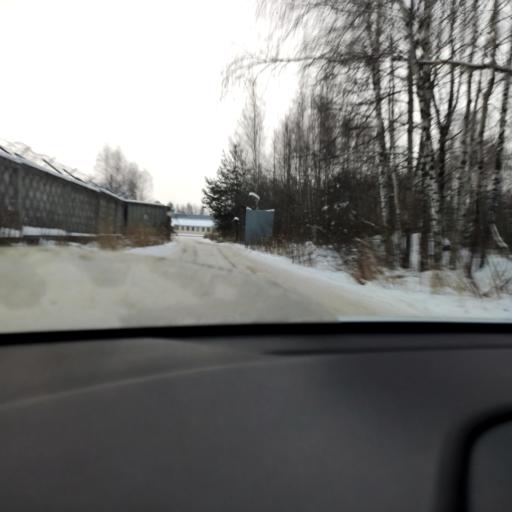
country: RU
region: Tatarstan
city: Osinovo
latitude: 55.8903
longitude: 48.8275
